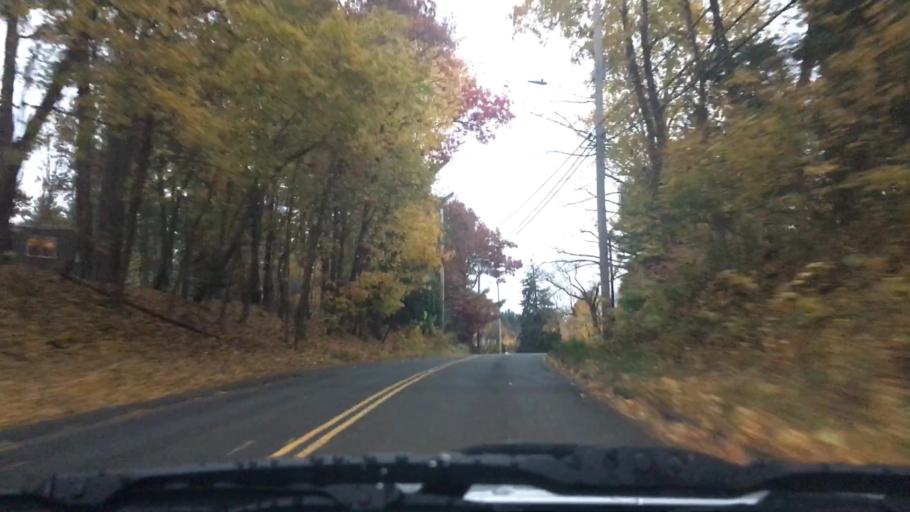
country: US
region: Massachusetts
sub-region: Hampden County
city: Westfield
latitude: 42.1252
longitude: -72.7780
